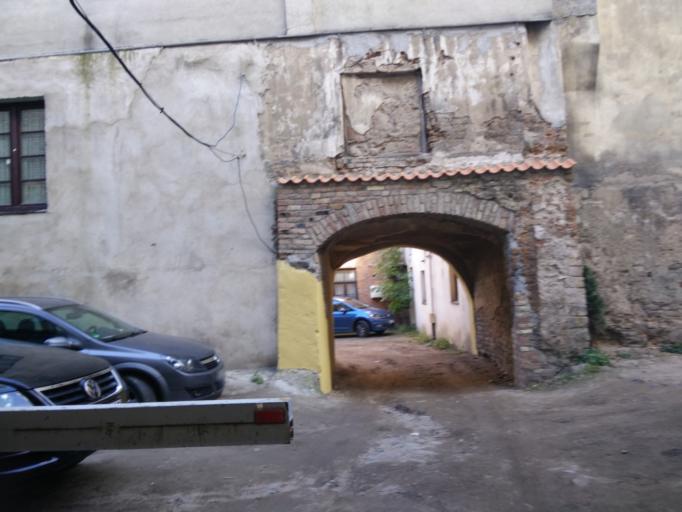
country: LT
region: Vilnius County
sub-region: Vilnius
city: Vilnius
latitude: 54.6791
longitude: 25.2821
